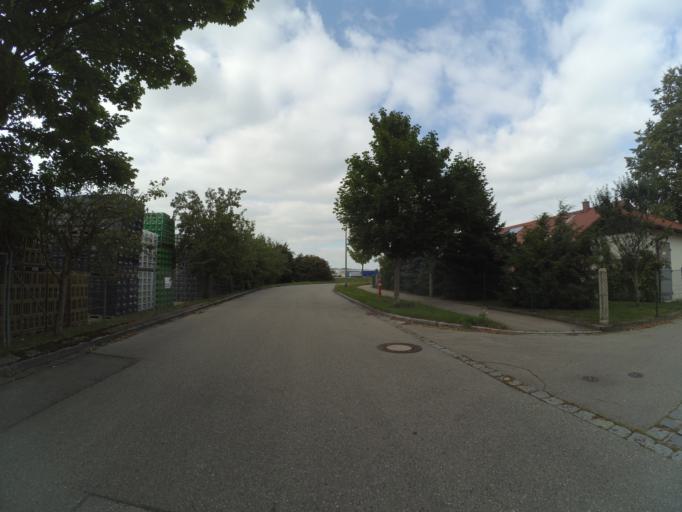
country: DE
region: Bavaria
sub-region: Swabia
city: Buchloe
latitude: 48.0402
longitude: 10.7112
